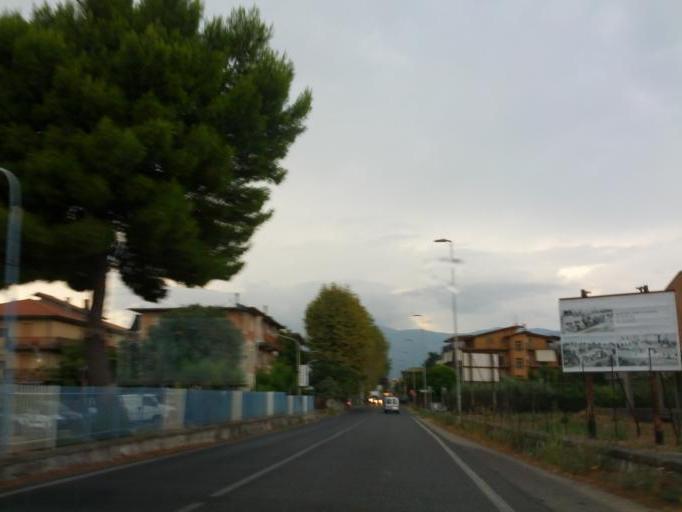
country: IT
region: Latium
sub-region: Provincia di Latina
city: Fondi
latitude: 41.3478
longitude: 13.4419
